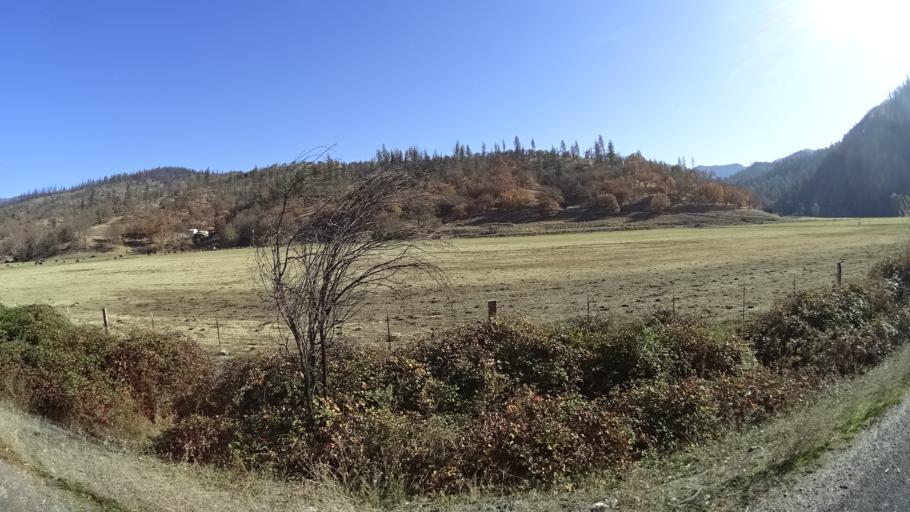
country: US
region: California
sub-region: Siskiyou County
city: Happy Camp
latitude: 41.8273
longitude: -123.0056
